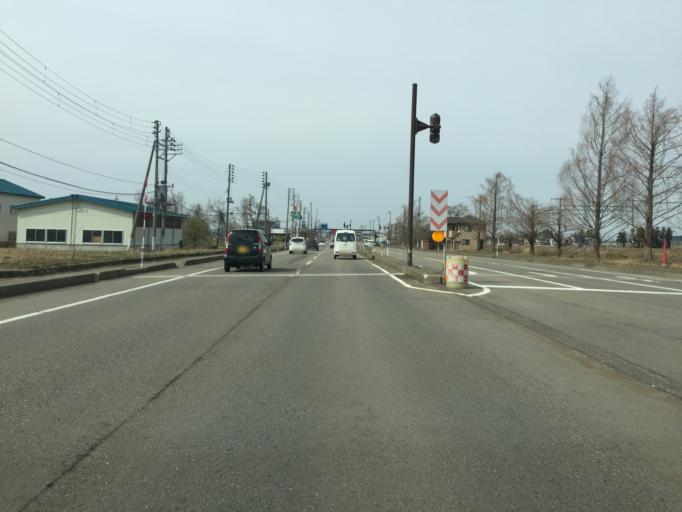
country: JP
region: Niigata
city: Nagaoka
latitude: 37.3747
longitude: 138.8345
